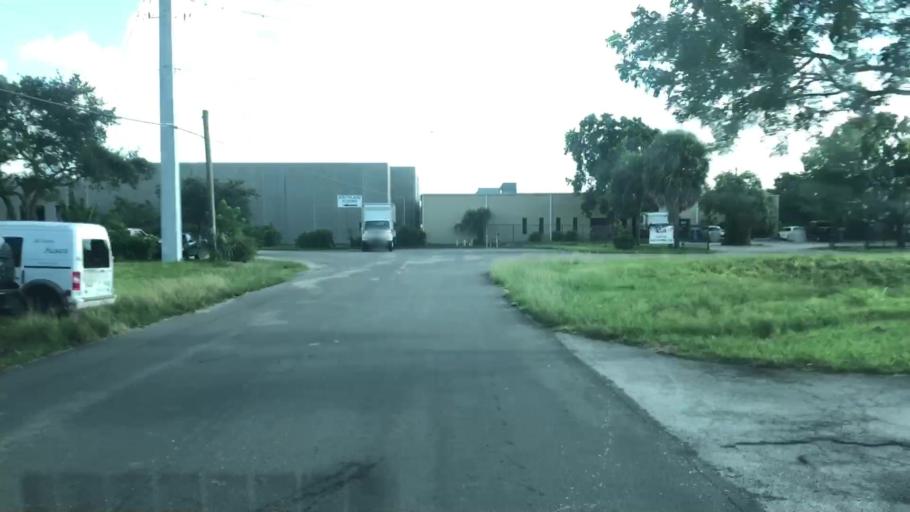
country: US
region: Florida
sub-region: Broward County
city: Kendall Green
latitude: 26.2637
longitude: -80.1478
